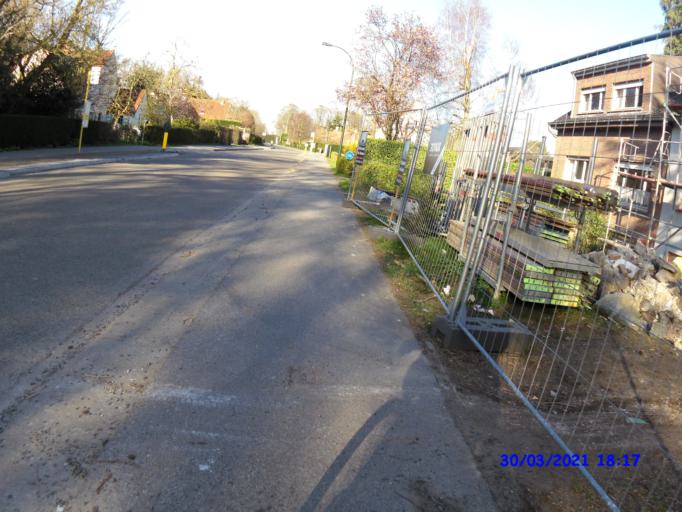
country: BE
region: Flanders
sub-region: Provincie Oost-Vlaanderen
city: Sint-Martens-Latem
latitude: 51.0211
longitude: 3.6458
